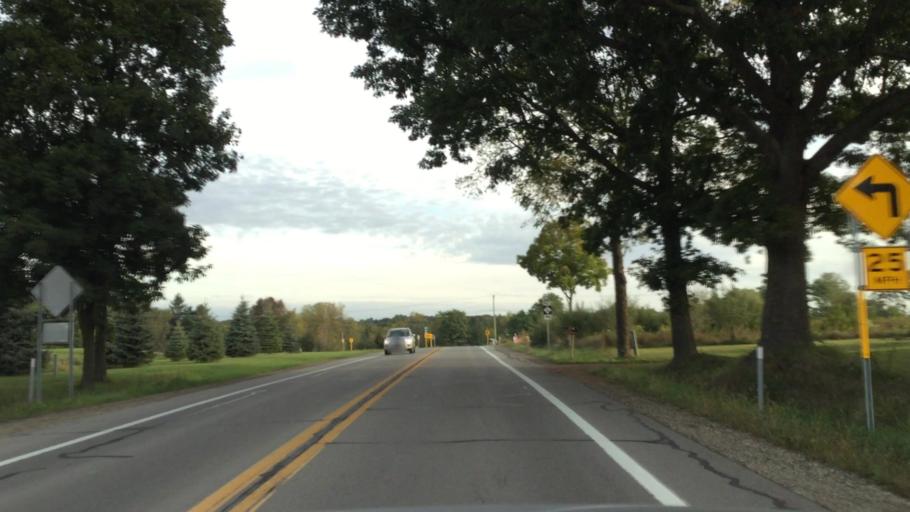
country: US
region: Michigan
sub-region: Livingston County
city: Whitmore Lake
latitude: 42.4505
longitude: -83.7852
